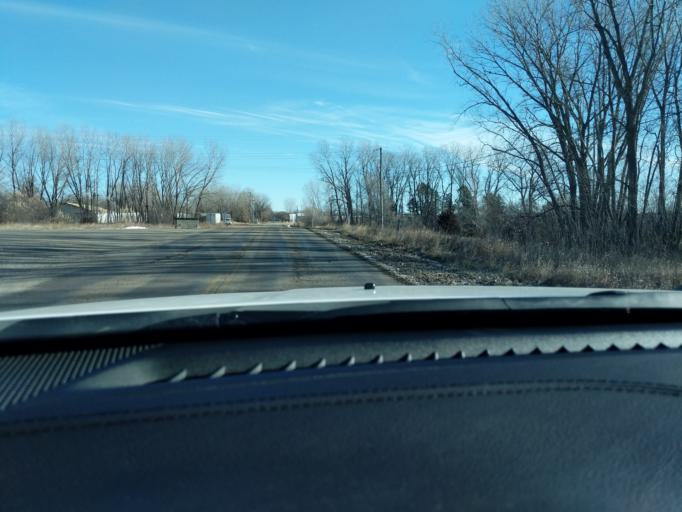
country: US
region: Minnesota
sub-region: Yellow Medicine County
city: Granite Falls
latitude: 44.8081
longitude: -95.5715
